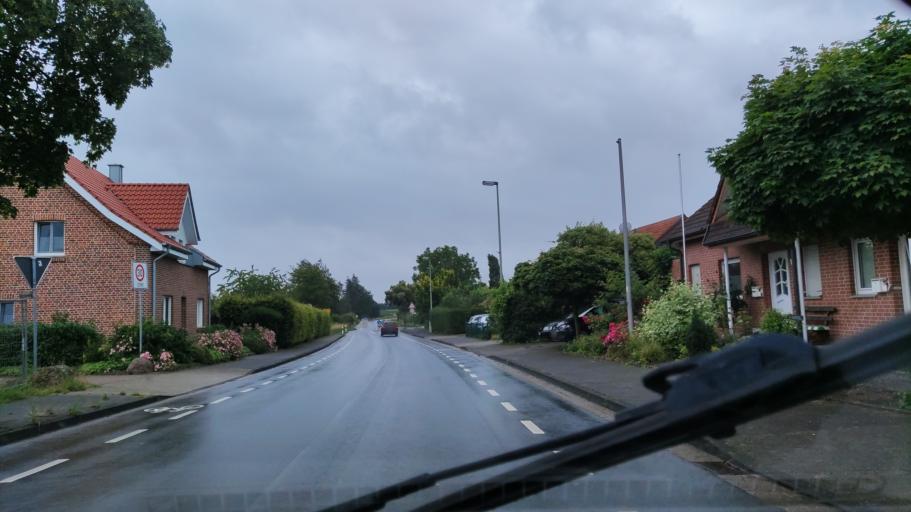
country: DE
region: North Rhine-Westphalia
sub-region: Regierungsbezirk Munster
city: Everswinkel
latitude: 51.9117
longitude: 7.8111
